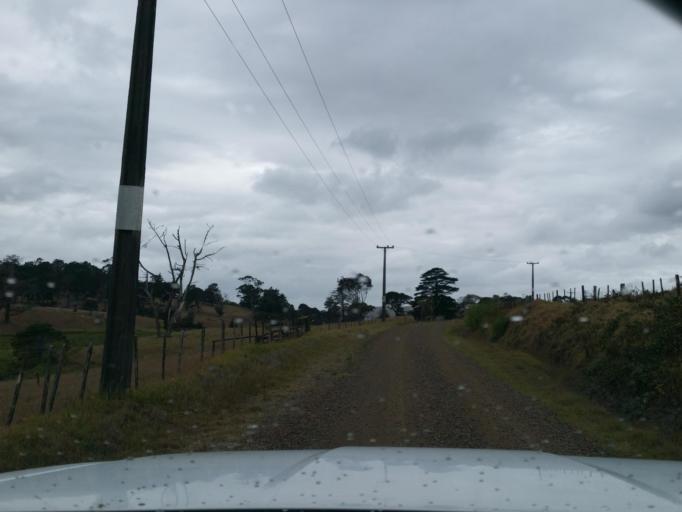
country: NZ
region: Auckland
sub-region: Auckland
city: Wellsford
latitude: -36.2545
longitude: 174.2374
